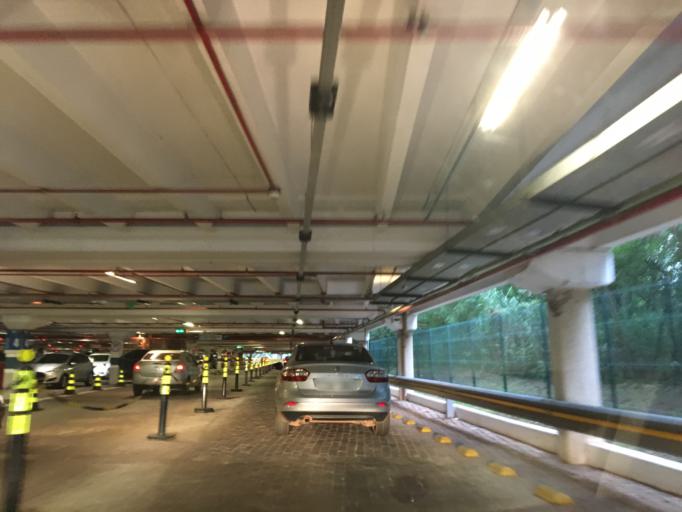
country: BR
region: Federal District
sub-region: Brasilia
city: Brasilia
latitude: -15.8318
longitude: -47.9576
